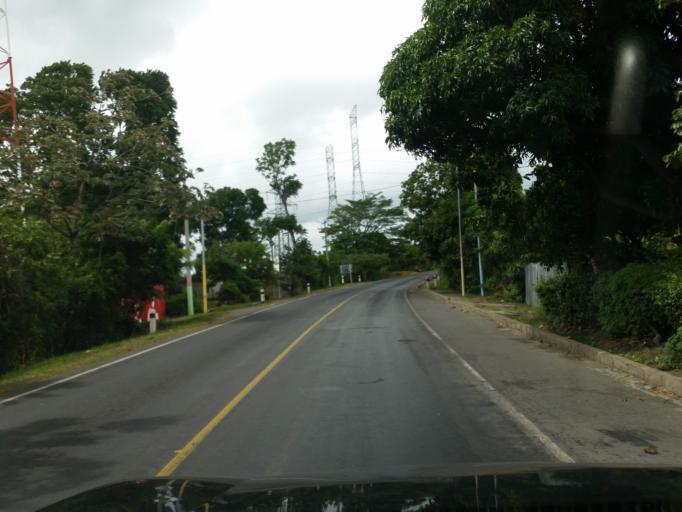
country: NI
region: Managua
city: El Crucero
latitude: 12.0417
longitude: -86.3110
